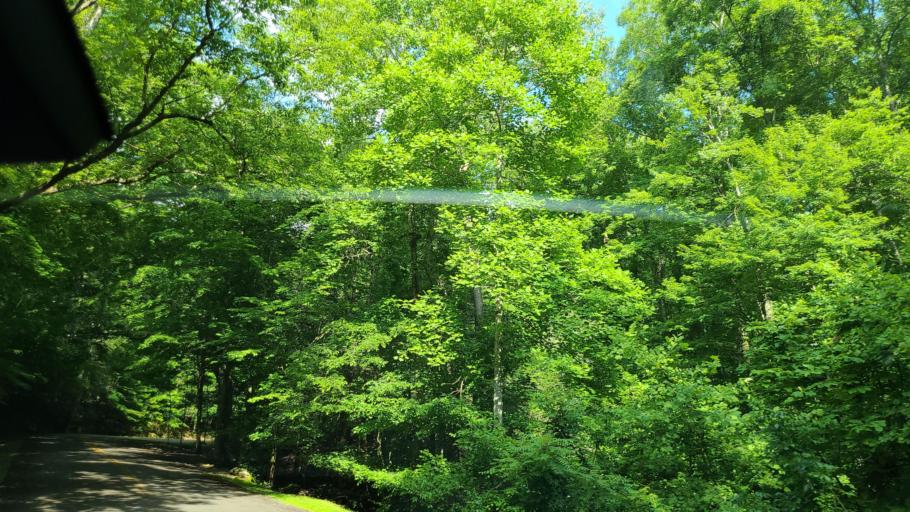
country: US
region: Kentucky
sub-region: Bell County
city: Pineville
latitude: 36.7408
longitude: -83.7082
